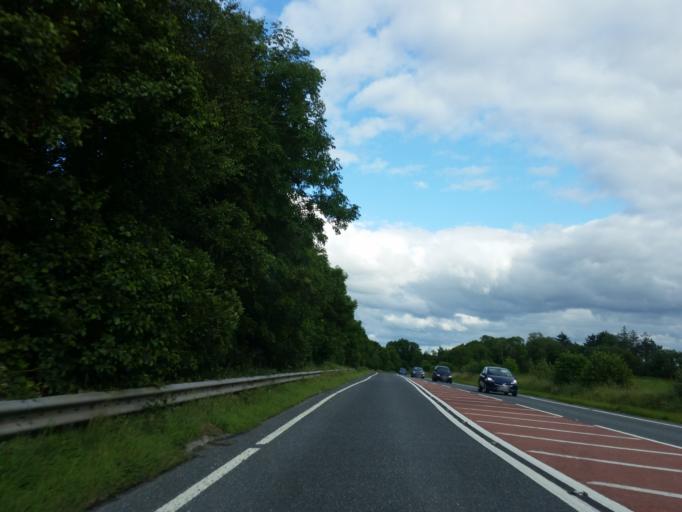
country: GB
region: Northern Ireland
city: Lisnaskea
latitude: 54.3130
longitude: -7.5059
